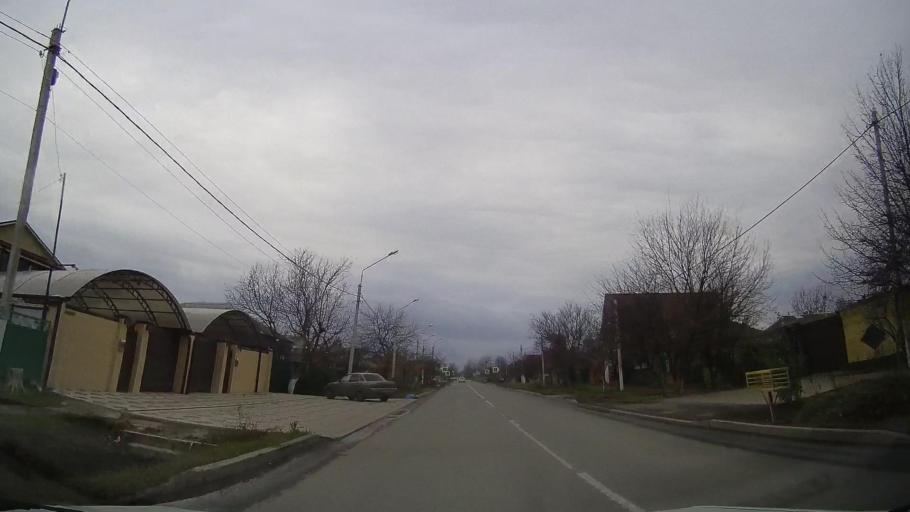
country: RU
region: Rostov
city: Bataysk
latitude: 47.1232
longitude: 39.7435
